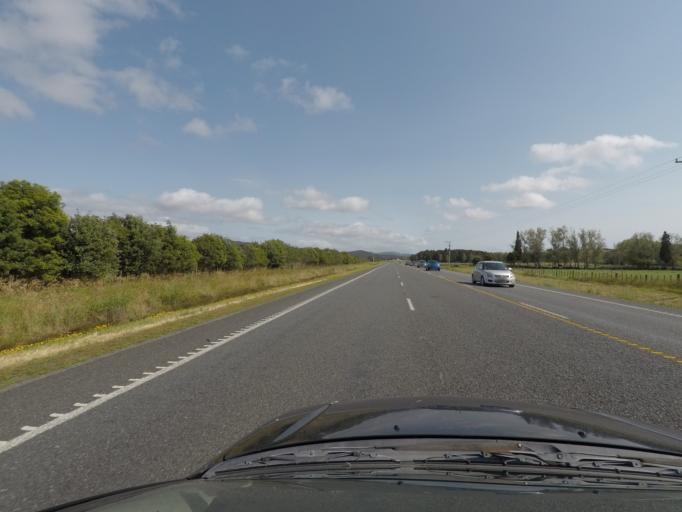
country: NZ
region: Northland
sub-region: Whangarei
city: Ruakaka
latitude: -36.0151
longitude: 174.4184
